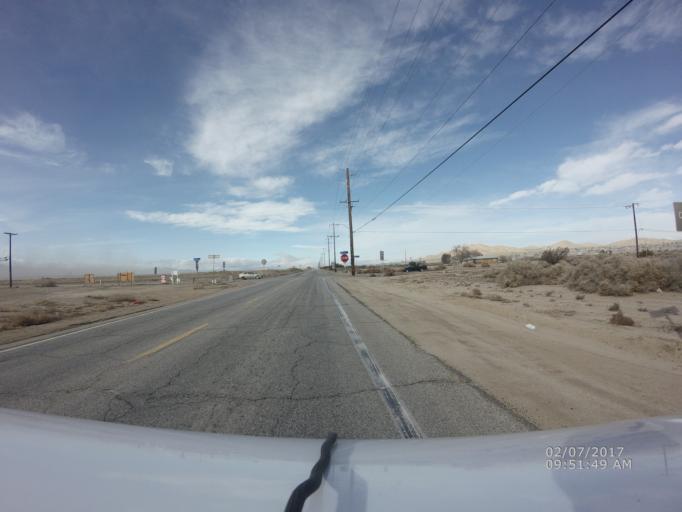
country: US
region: California
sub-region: Los Angeles County
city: Lake Los Angeles
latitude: 34.5799
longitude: -117.8261
